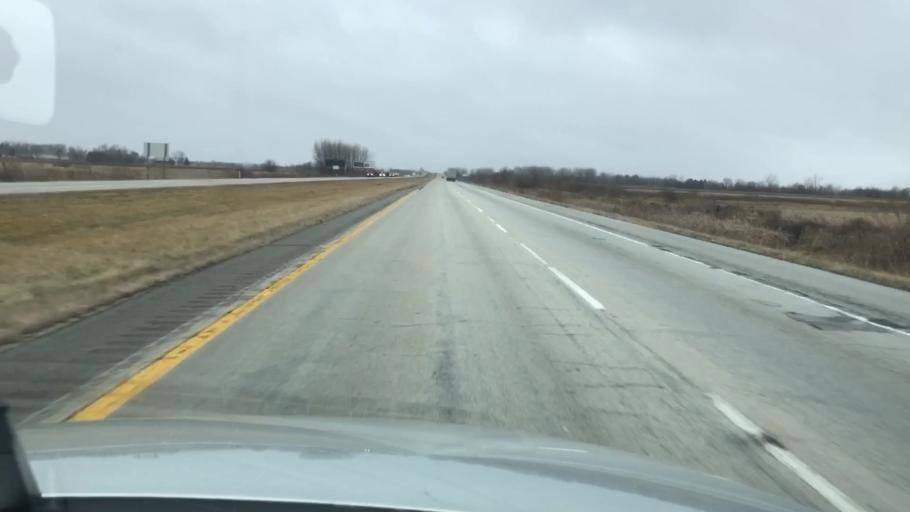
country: US
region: Indiana
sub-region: Starke County
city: Knox
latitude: 41.3940
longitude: -86.6050
